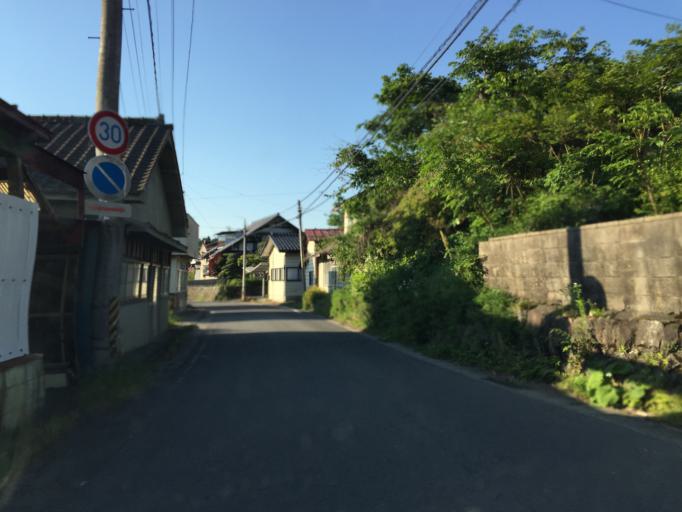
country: JP
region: Ibaraki
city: Daigo
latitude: 36.9331
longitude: 140.4462
